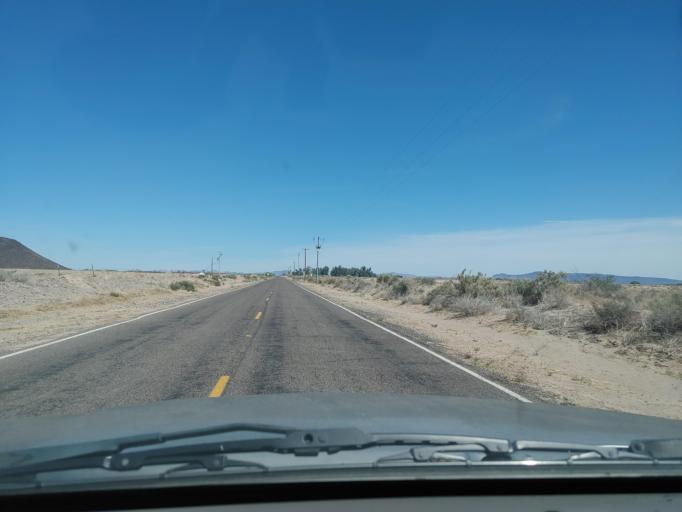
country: US
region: Arizona
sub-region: Maricopa County
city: Gila Bend
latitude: 32.9806
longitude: -113.3060
